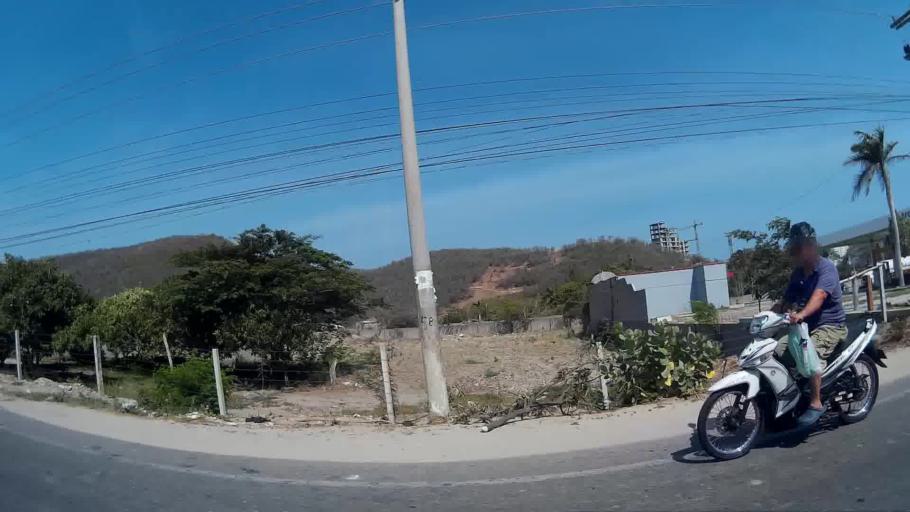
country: CO
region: Magdalena
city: Santa Marta
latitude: 11.1857
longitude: -74.2253
